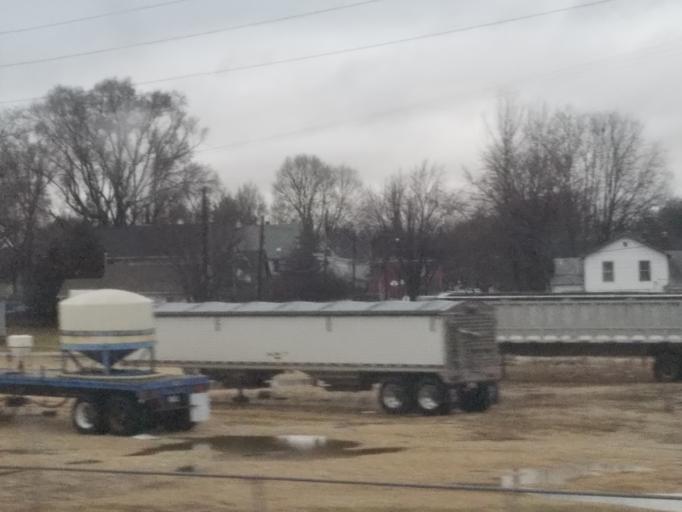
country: US
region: Illinois
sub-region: Warren County
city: Monmouth
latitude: 40.9049
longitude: -90.6419
